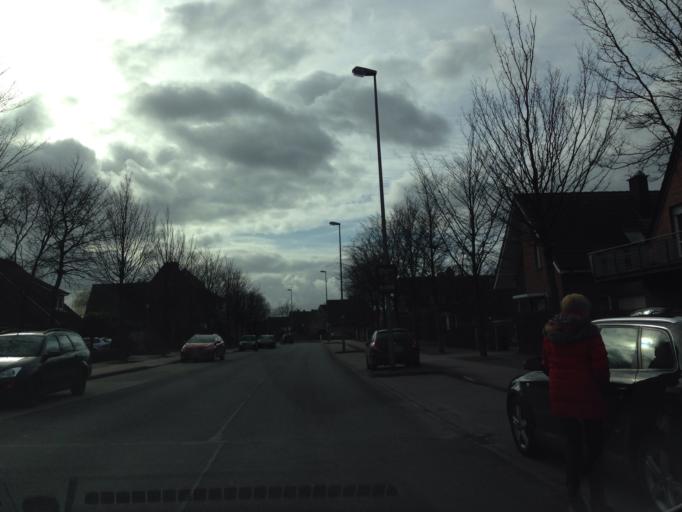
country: DE
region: North Rhine-Westphalia
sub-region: Regierungsbezirk Munster
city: Muenster
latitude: 51.9945
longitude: 7.6007
